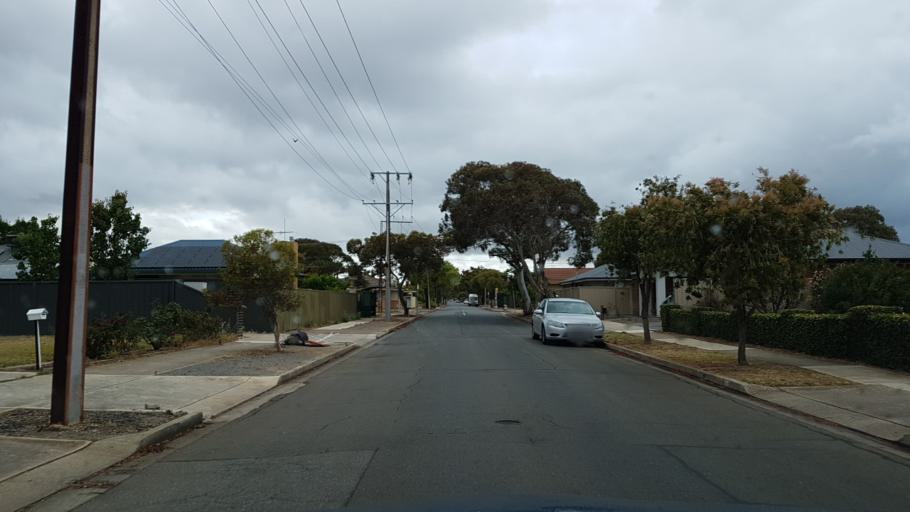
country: AU
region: South Australia
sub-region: Marion
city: Plympton Park
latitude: -34.9741
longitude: 138.5490
